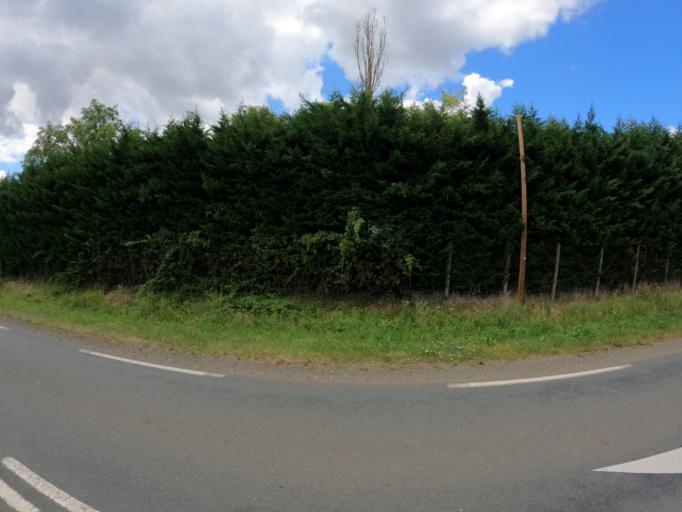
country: FR
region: Pays de la Loire
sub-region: Departement de la Sarthe
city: Juigne-sur-Sarthe
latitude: 47.8820
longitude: -0.2989
